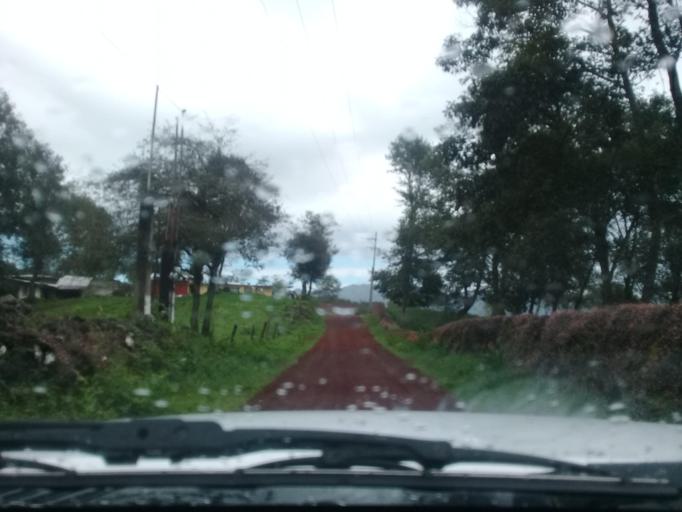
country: MX
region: Veracruz
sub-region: Acajete
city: La Joya
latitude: 19.6202
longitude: -97.0005
